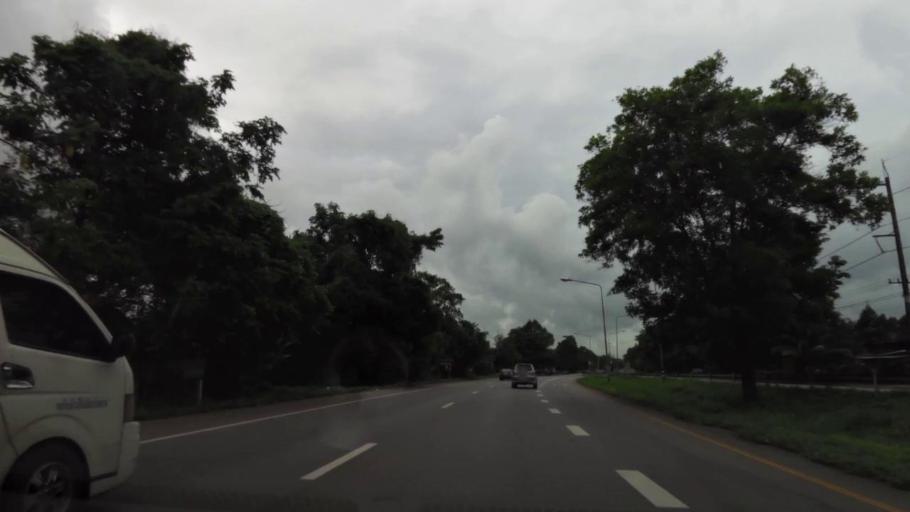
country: TH
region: Chanthaburi
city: Tha Mai
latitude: 12.6483
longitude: 102.0226
